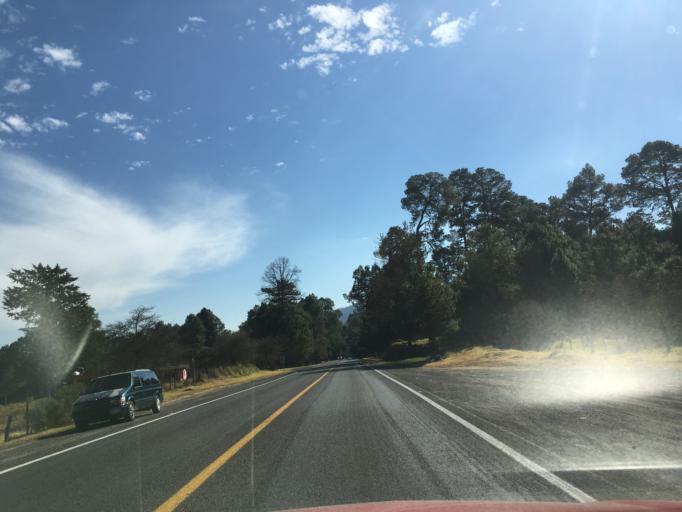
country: MX
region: Michoacan
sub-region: Hidalgo
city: Tierras Coloradas (San Pedro)
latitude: 19.6693
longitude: -100.6904
